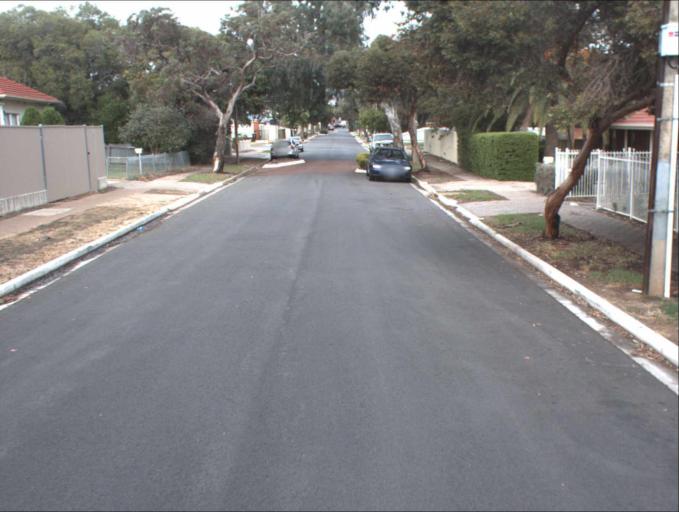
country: AU
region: South Australia
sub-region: Port Adelaide Enfield
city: Gilles Plains
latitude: -34.8524
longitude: 138.6574
